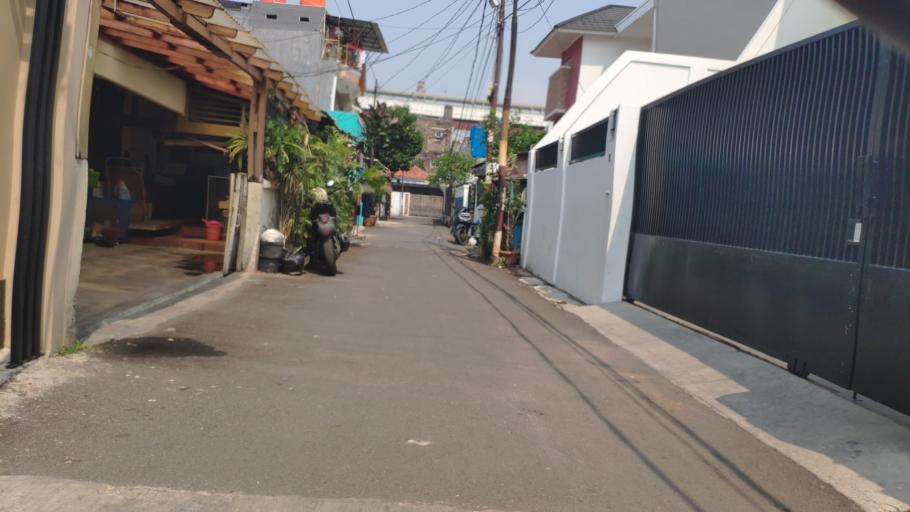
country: ID
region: Jakarta Raya
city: Jakarta
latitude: -6.2556
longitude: 106.7958
